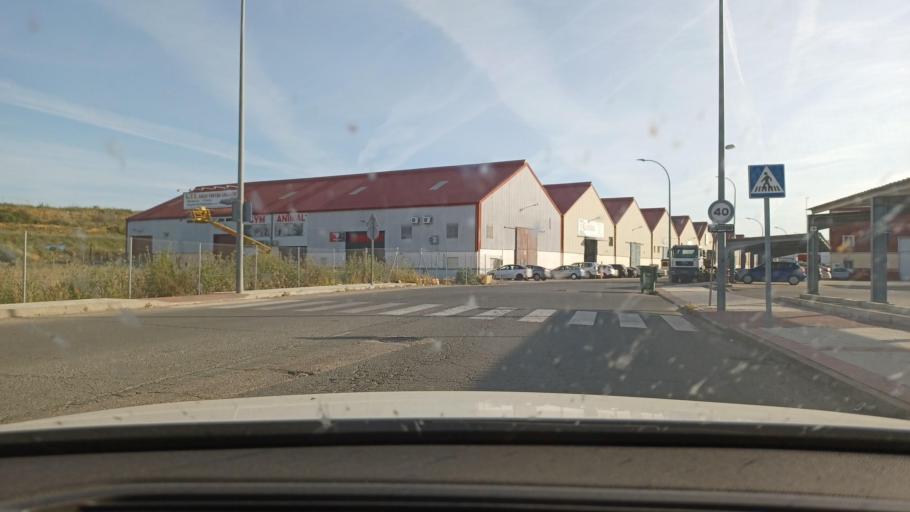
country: ES
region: Castille-La Mancha
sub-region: Provincia de Guadalajara
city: Alovera
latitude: 40.5933
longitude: -3.2362
